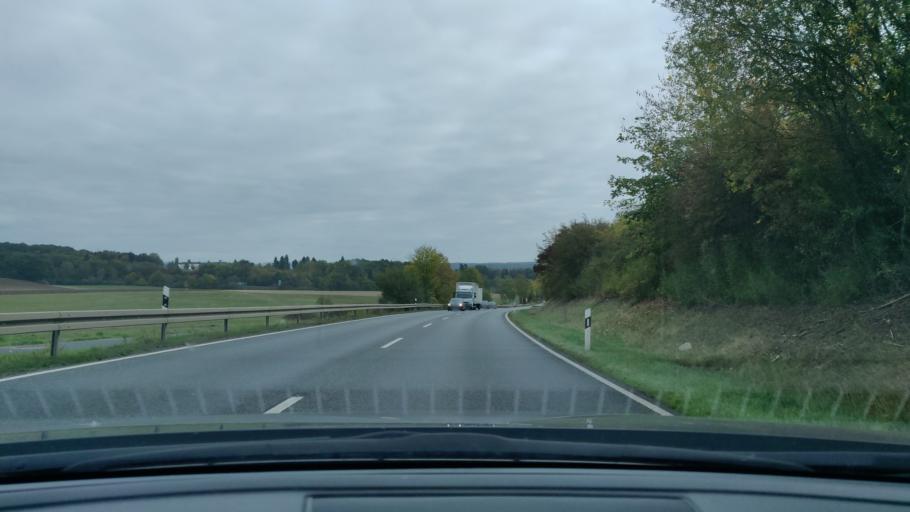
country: DE
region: Hesse
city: Schwalmstadt
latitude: 50.9223
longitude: 9.2427
